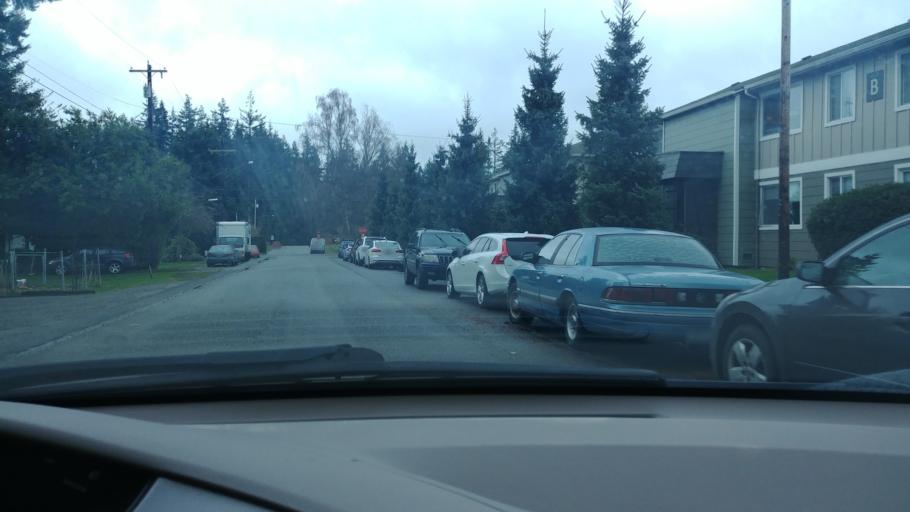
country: US
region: Washington
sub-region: Snohomish County
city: Everett
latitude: 47.9559
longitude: -122.2197
